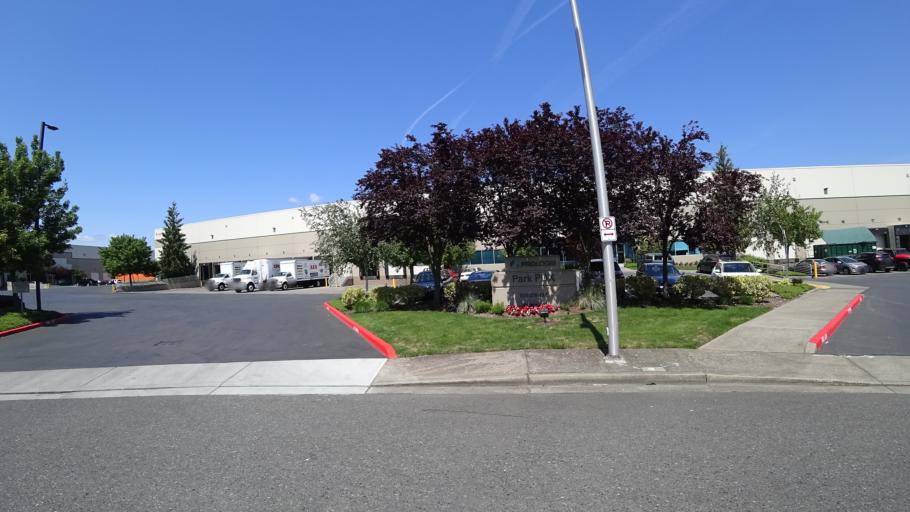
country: US
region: Oregon
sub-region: Multnomah County
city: Fairview
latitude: 45.5607
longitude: -122.5050
